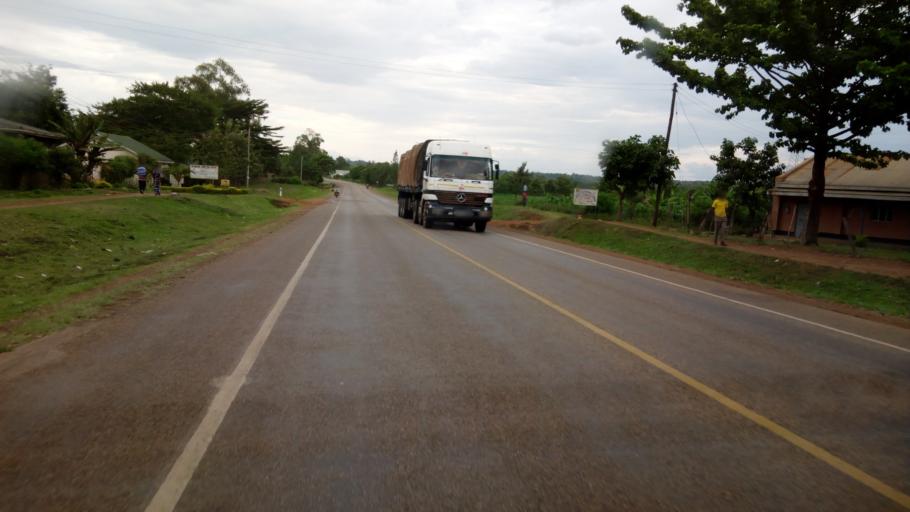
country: UG
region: Eastern Region
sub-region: Mbale District
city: Mbale
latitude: 1.0061
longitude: 34.1698
